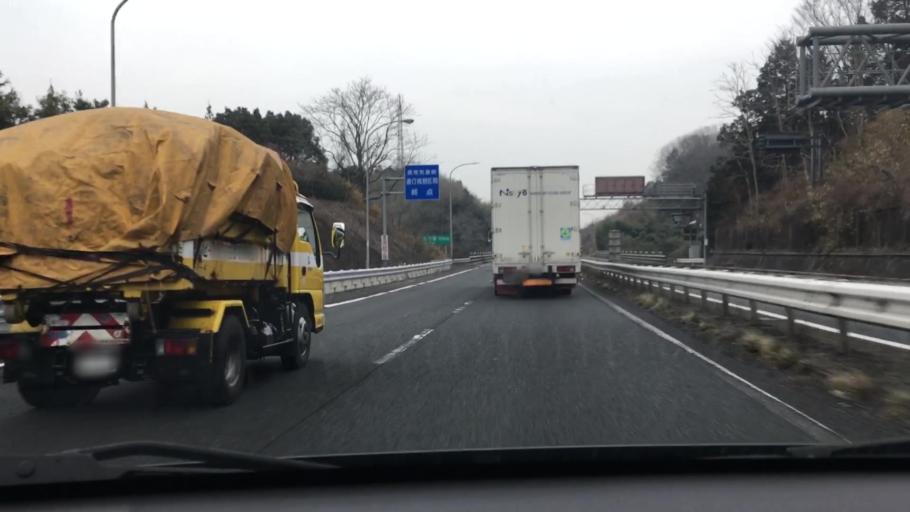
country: JP
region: Mie
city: Nabari
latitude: 34.6979
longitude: 136.0623
